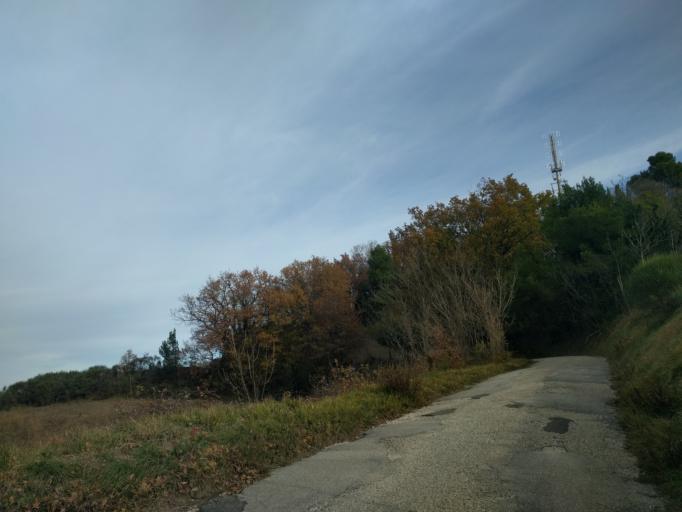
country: IT
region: The Marches
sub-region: Provincia di Pesaro e Urbino
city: Centinarola
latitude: 43.8173
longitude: 12.9719
